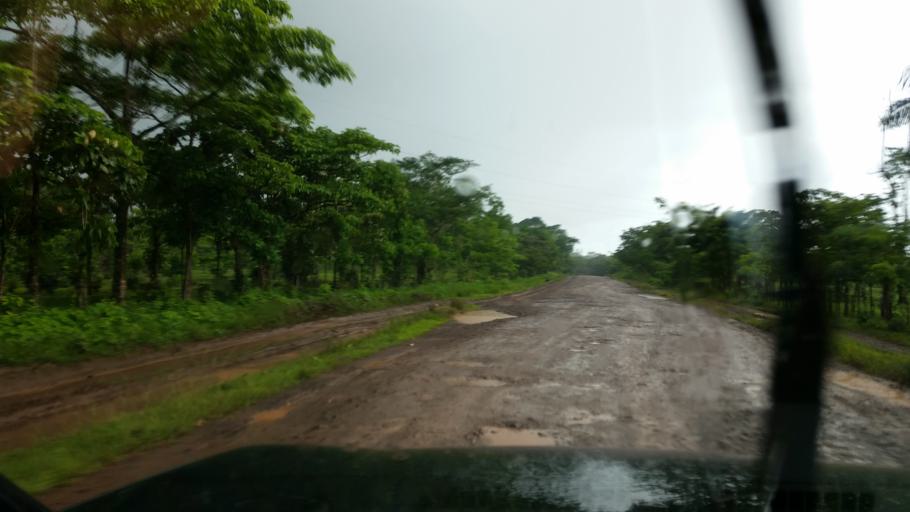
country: NI
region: Atlantico Norte (RAAN)
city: Siuna
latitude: 13.3960
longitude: -84.8552
